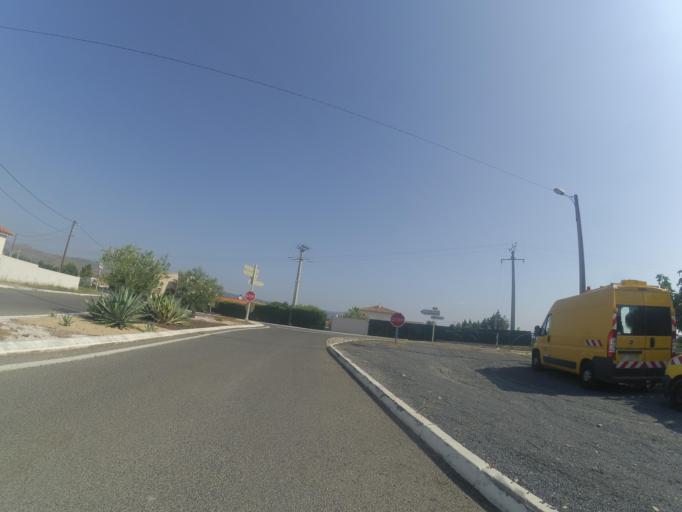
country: FR
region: Languedoc-Roussillon
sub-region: Departement des Pyrenees-Orientales
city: Ille-sur-Tet
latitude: 42.6554
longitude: 2.6235
